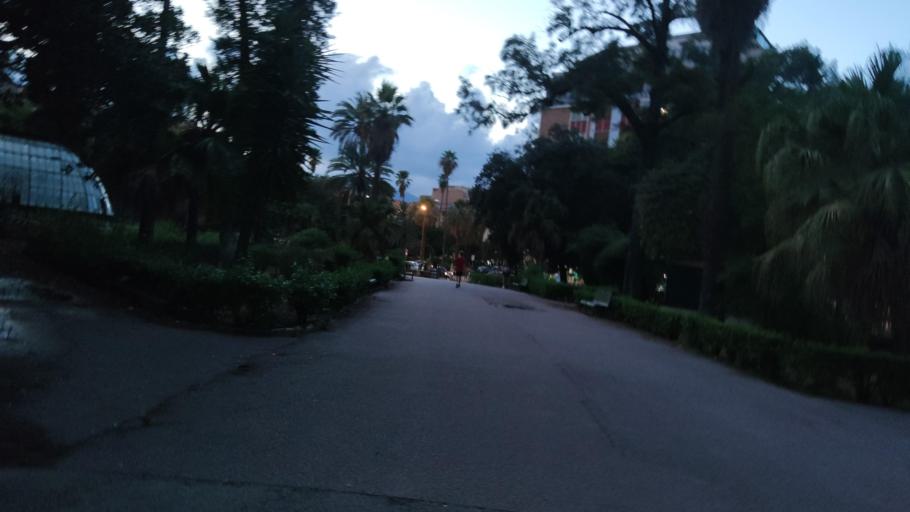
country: IT
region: Sicily
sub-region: Palermo
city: Palermo
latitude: 38.1335
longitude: 13.3515
